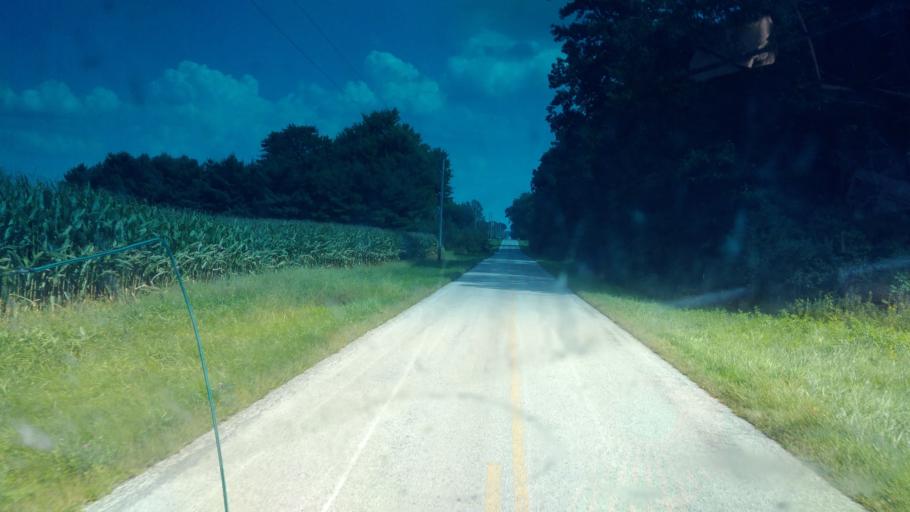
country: US
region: Ohio
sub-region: Hardin County
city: Ada
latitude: 40.7186
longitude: -83.8178
